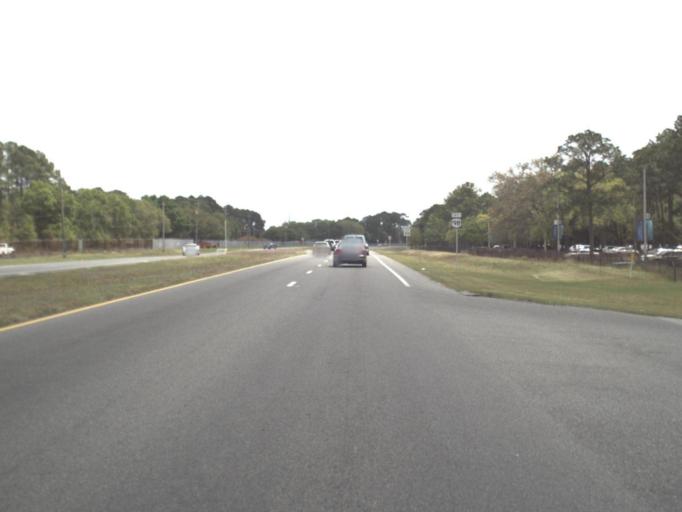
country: US
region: Florida
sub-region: Escambia County
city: Warrington
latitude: 30.3974
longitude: -87.2861
